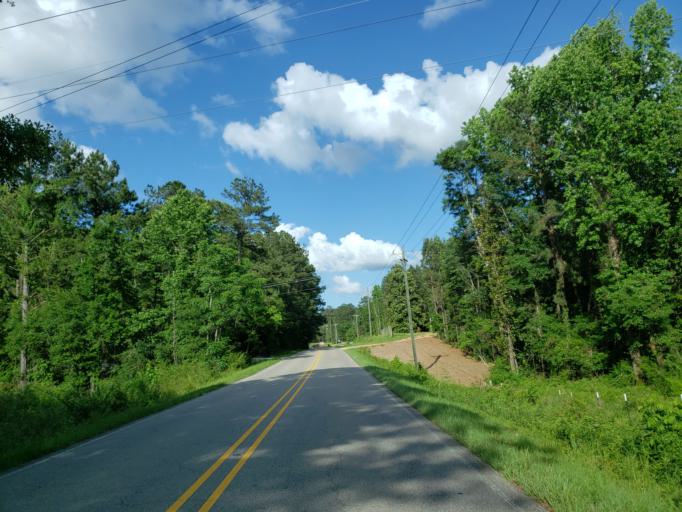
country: US
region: Mississippi
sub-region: Lamar County
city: West Hattiesburg
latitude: 31.2876
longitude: -89.4599
